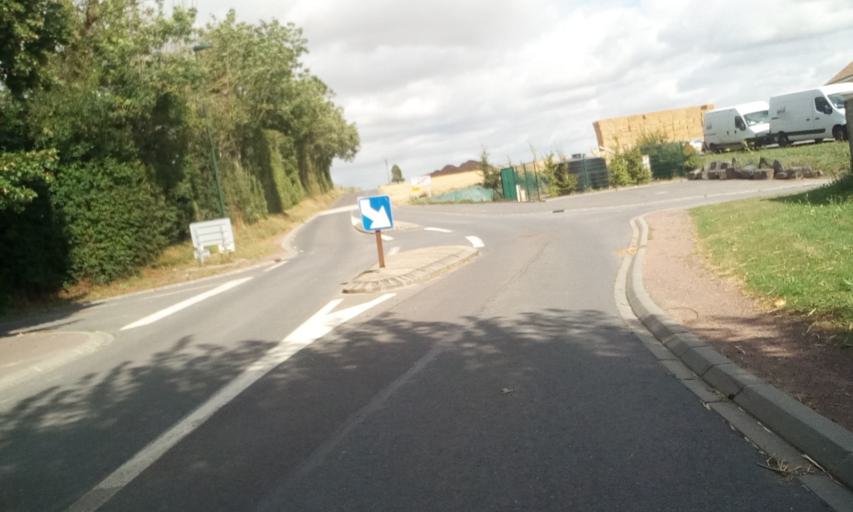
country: FR
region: Lower Normandy
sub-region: Departement du Calvados
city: Cheux
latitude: 49.1962
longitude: -0.5388
